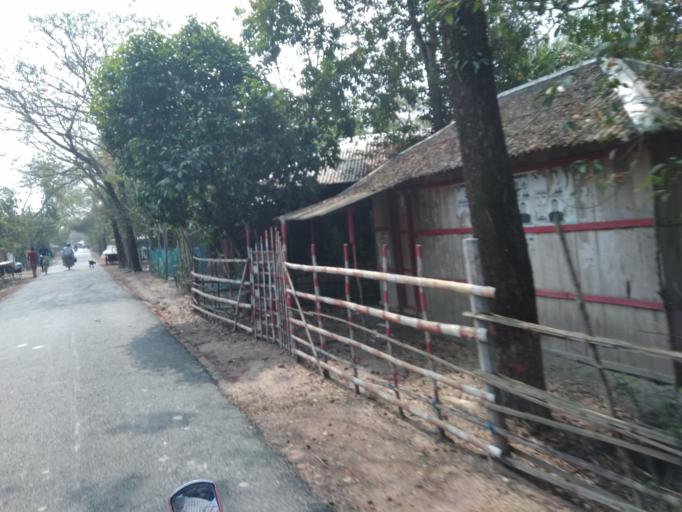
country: IN
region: West Bengal
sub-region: North 24 Parganas
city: Gosaba
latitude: 22.2666
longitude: 89.2177
